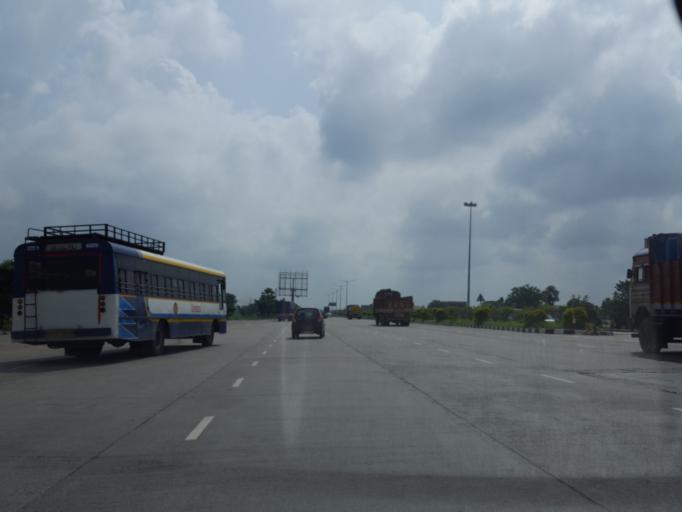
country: IN
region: Telangana
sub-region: Nalgonda
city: Bhongir
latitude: 17.2327
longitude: 78.9619
